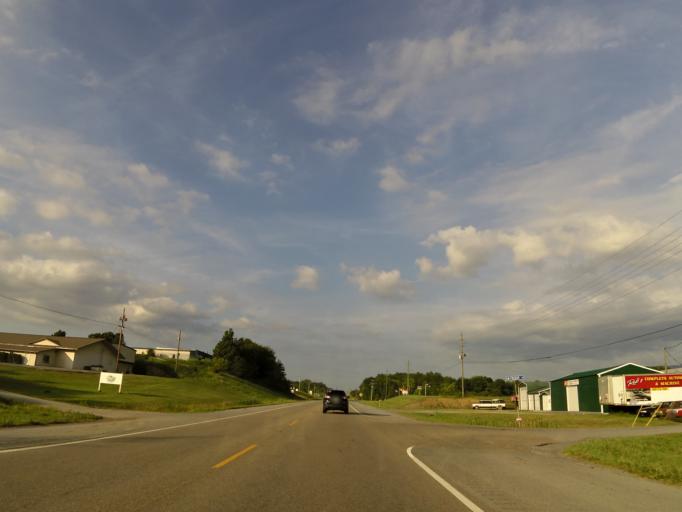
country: US
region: Tennessee
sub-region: Jefferson County
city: Dandridge
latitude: 35.8962
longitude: -83.4329
